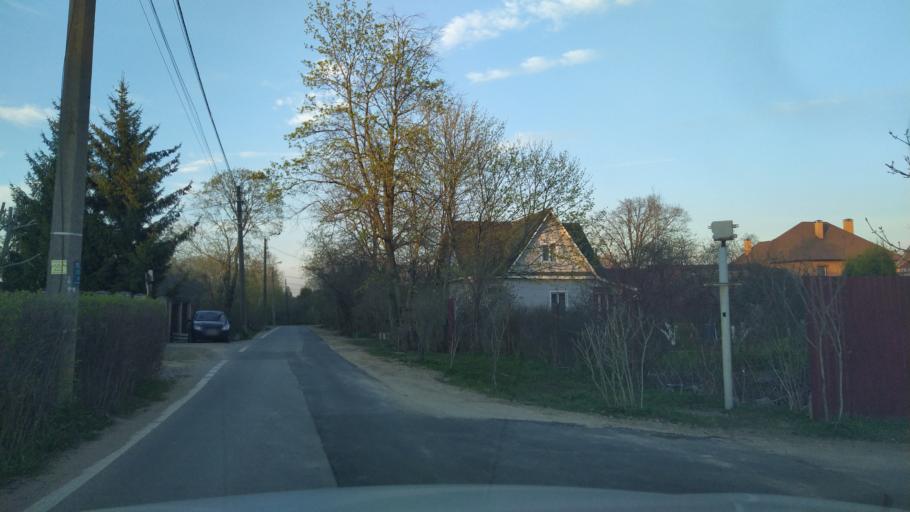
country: RU
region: St.-Petersburg
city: Pavlovsk
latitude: 59.6919
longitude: 30.4133
